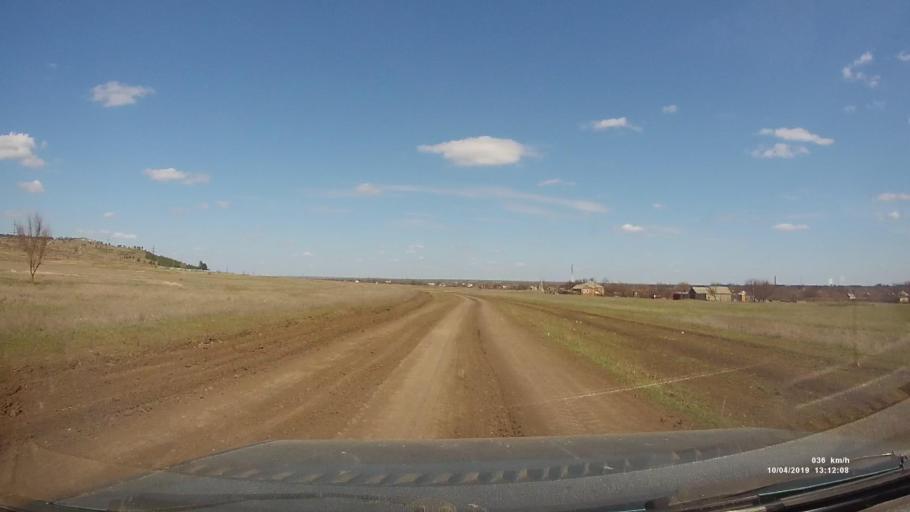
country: RU
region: Rostov
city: Masalovka
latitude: 48.4115
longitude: 40.2529
